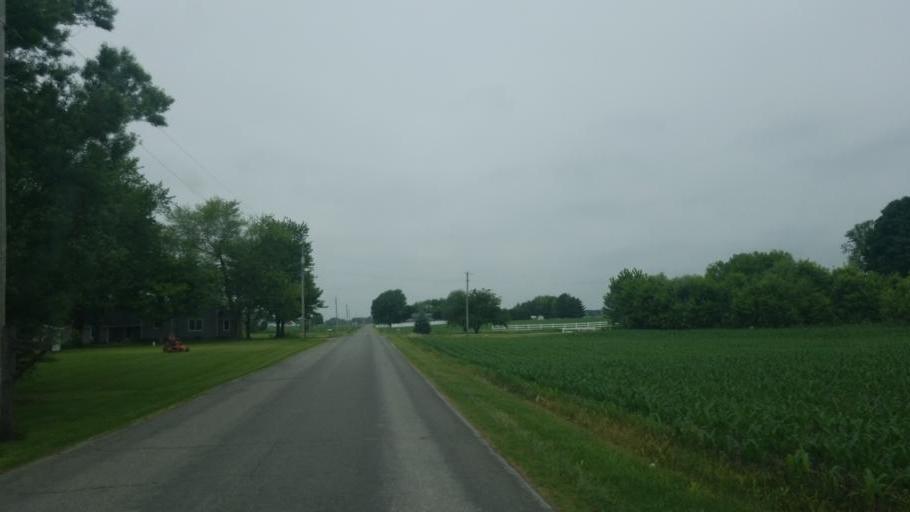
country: US
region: Indiana
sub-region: Elkhart County
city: Nappanee
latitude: 41.4718
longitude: -86.0259
